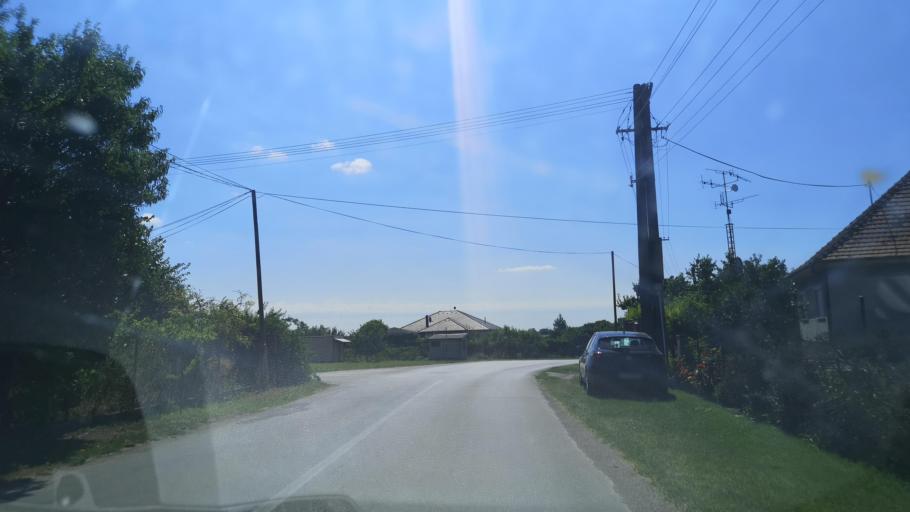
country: SK
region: Bratislavsky
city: Senec
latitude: 48.0998
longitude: 17.4785
